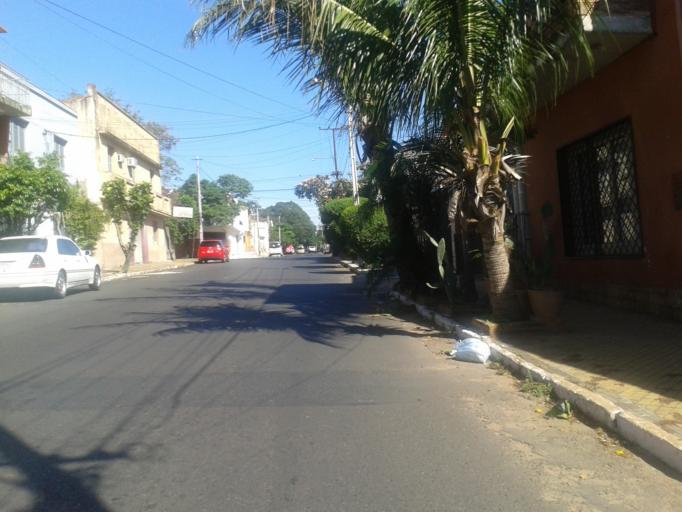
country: PY
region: Asuncion
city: Asuncion
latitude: -25.2944
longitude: -57.6368
